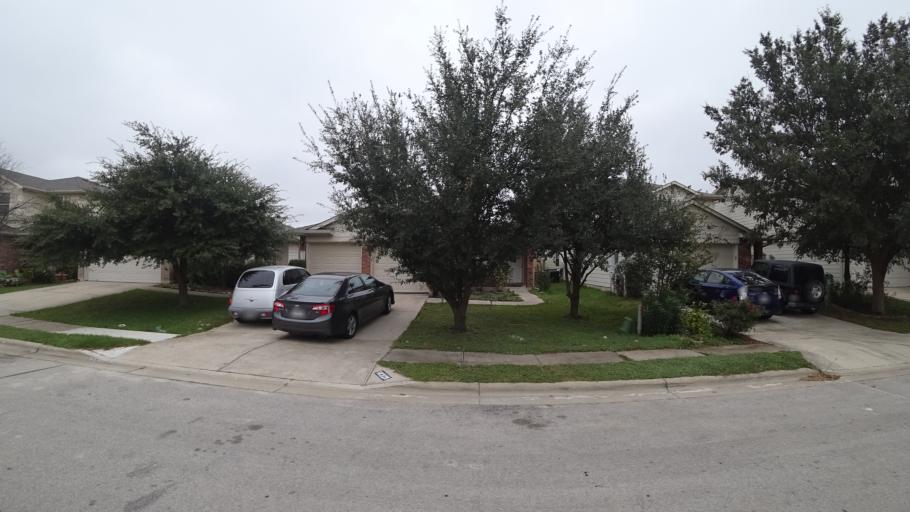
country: US
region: Texas
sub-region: Travis County
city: Manor
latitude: 30.3700
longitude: -97.6148
